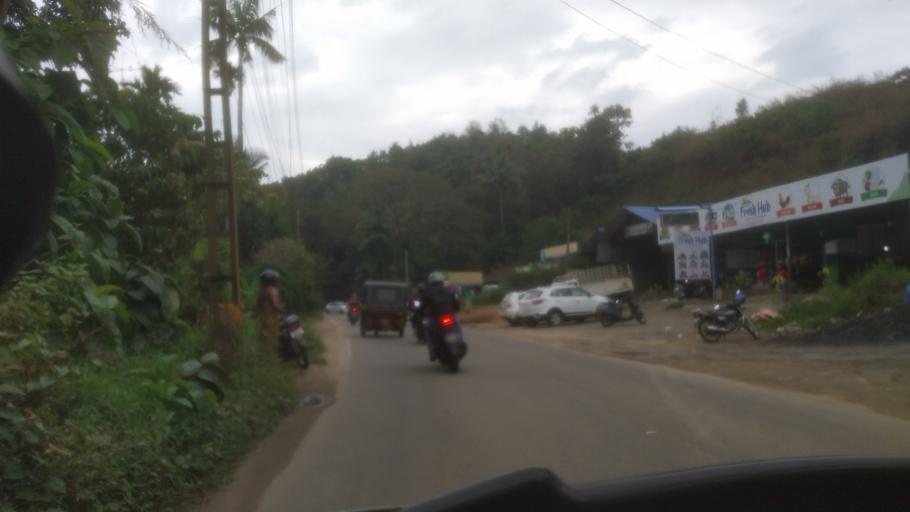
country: IN
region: Kerala
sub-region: Idukki
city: Munnar
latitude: 10.0063
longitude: 76.9633
